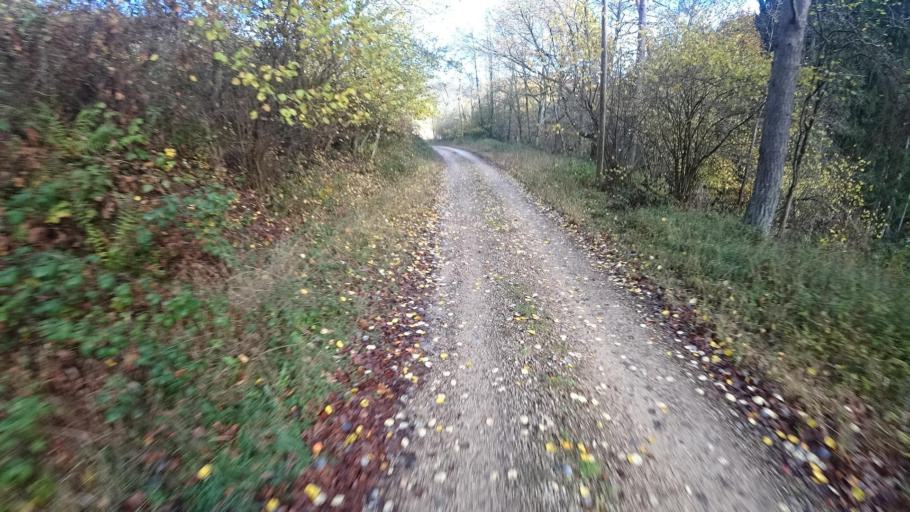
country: DE
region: Rheinland-Pfalz
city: Honningen
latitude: 50.4817
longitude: 6.9520
